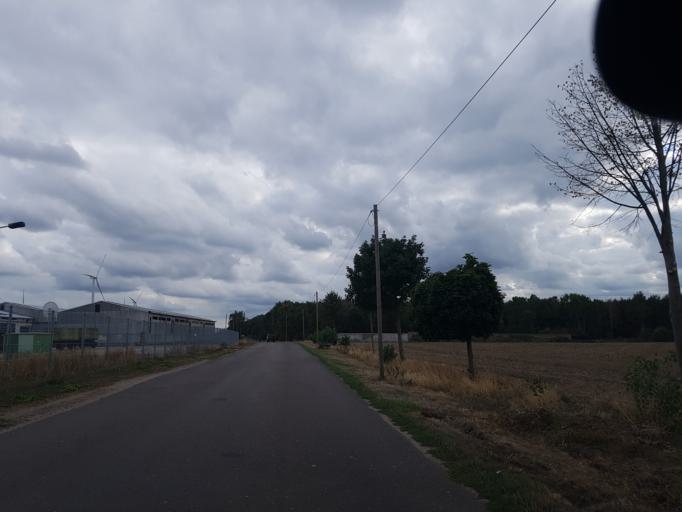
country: DE
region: Saxony-Anhalt
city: Klieken
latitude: 51.9506
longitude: 12.3104
